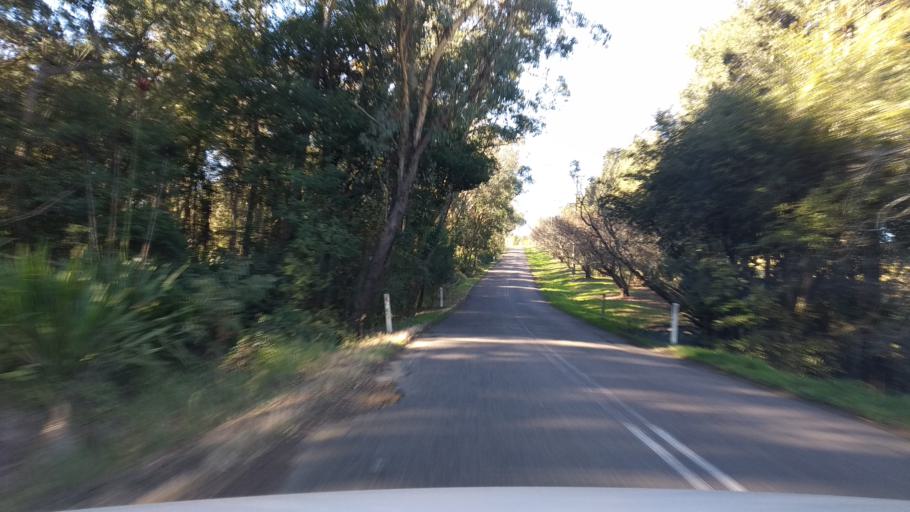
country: AU
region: New South Wales
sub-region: Wyong Shire
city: Little Jilliby
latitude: -33.2426
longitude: 151.2224
